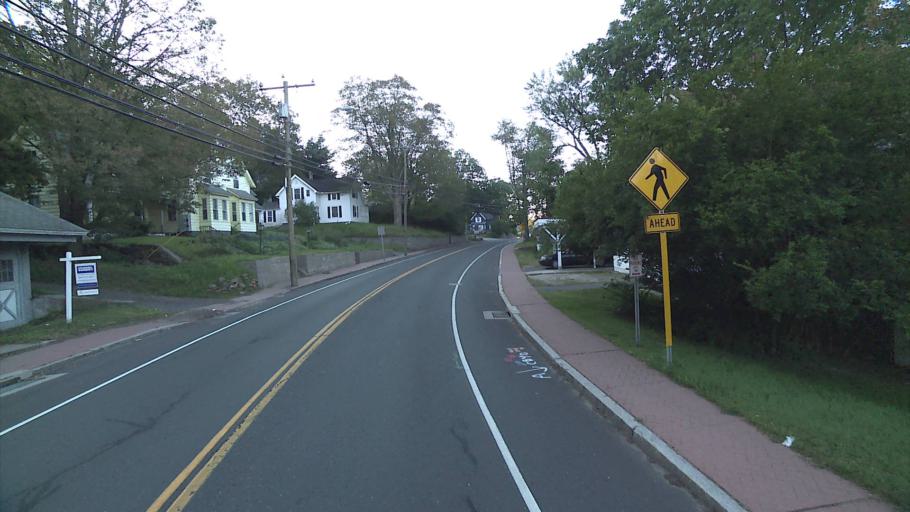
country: US
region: Connecticut
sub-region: Tolland County
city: Stafford Springs
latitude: 41.9585
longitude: -72.3115
